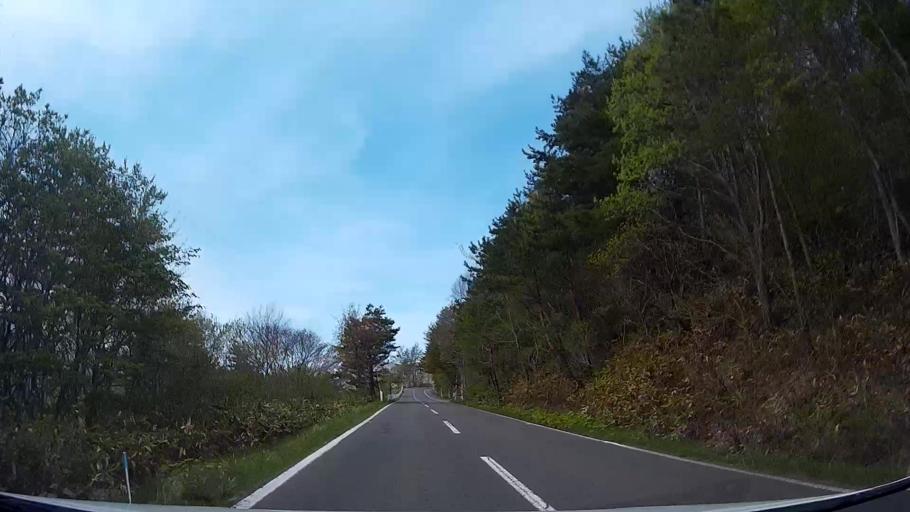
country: JP
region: Iwate
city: Shizukuishi
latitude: 39.9247
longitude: 140.9723
